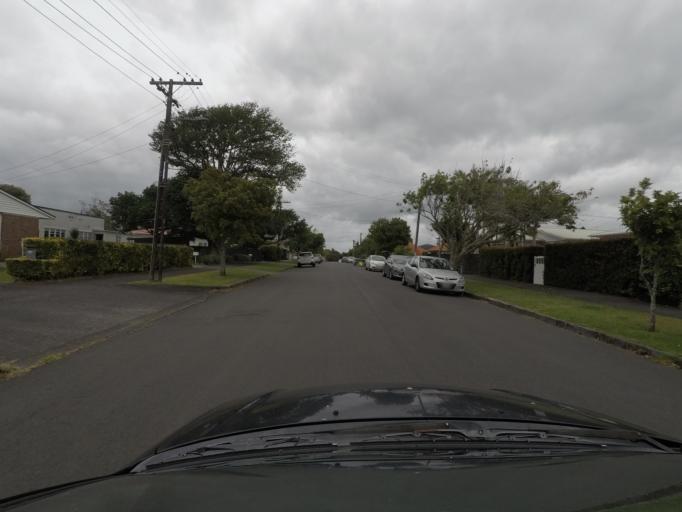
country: NZ
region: Auckland
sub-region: Auckland
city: Rosebank
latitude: -36.8684
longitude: 174.7024
